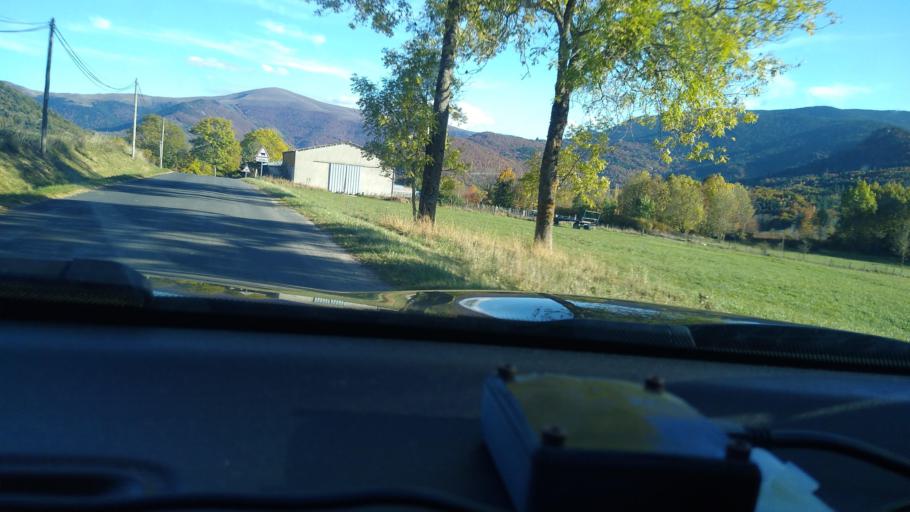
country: FR
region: Languedoc-Roussillon
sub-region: Departement de l'Aude
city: Quillan
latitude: 42.7452
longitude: 2.1872
